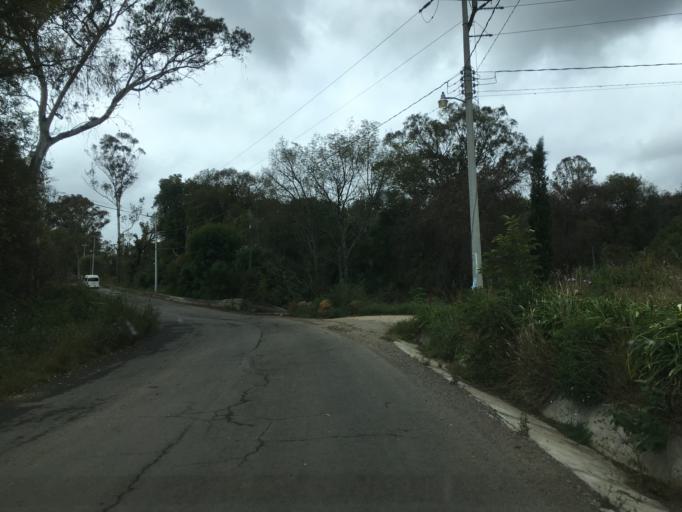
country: MX
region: Hidalgo
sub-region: Omitlan de Juarez
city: San Antonio el Paso
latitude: 20.2267
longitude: -98.5781
